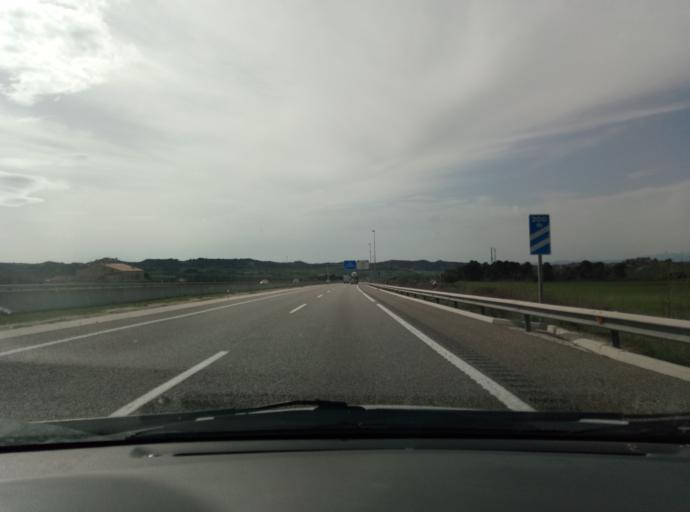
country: ES
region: Catalonia
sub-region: Provincia de Lleida
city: Sant Guim de Freixenet
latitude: 41.6311
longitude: 1.3549
